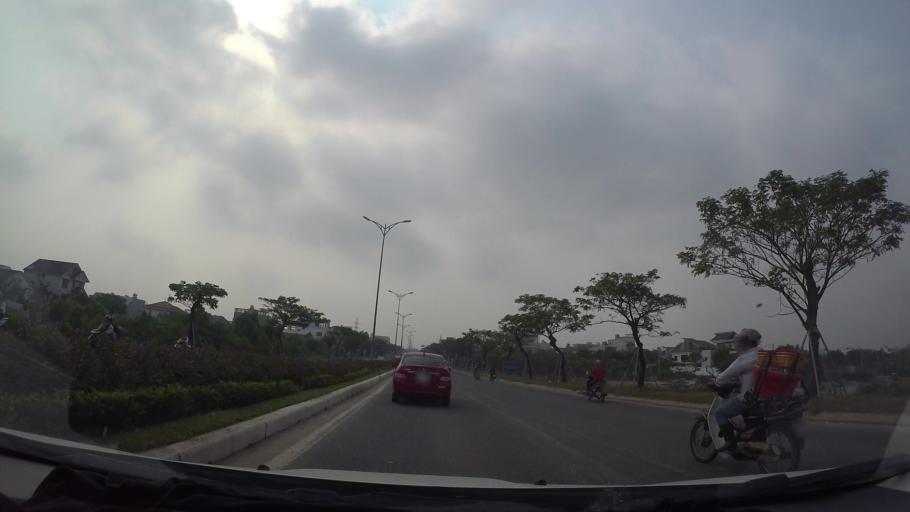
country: VN
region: Da Nang
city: Cam Le
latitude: 16.0120
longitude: 108.2162
